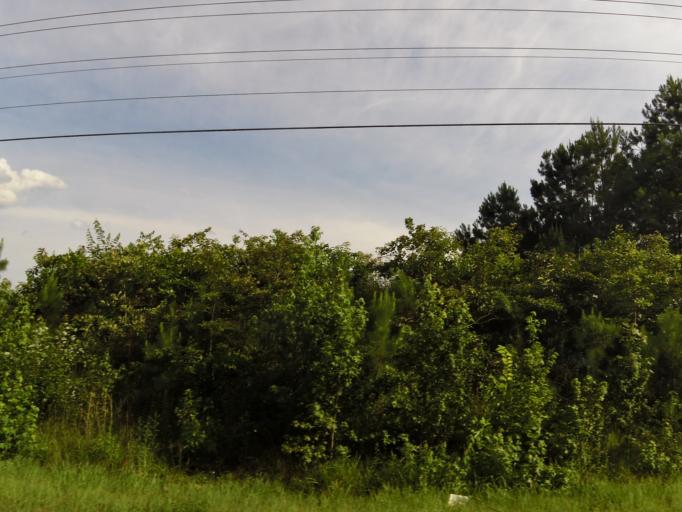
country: US
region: Tennessee
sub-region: Benton County
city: Camden
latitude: 36.0453
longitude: -88.1453
